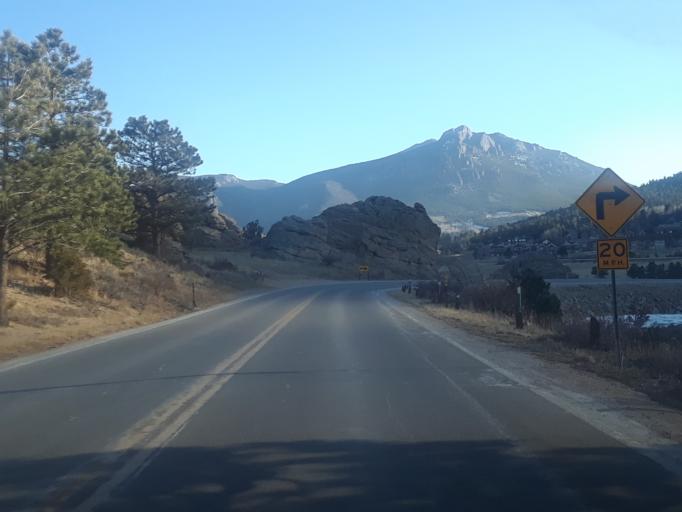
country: US
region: Colorado
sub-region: Larimer County
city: Estes Park
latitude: 40.3436
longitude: -105.5296
